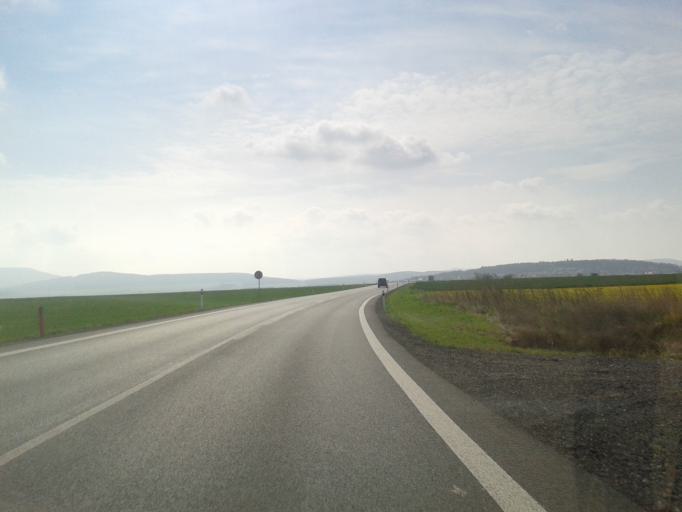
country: CZ
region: Central Bohemia
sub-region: Okres Beroun
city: Horovice
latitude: 49.8553
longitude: 13.9064
